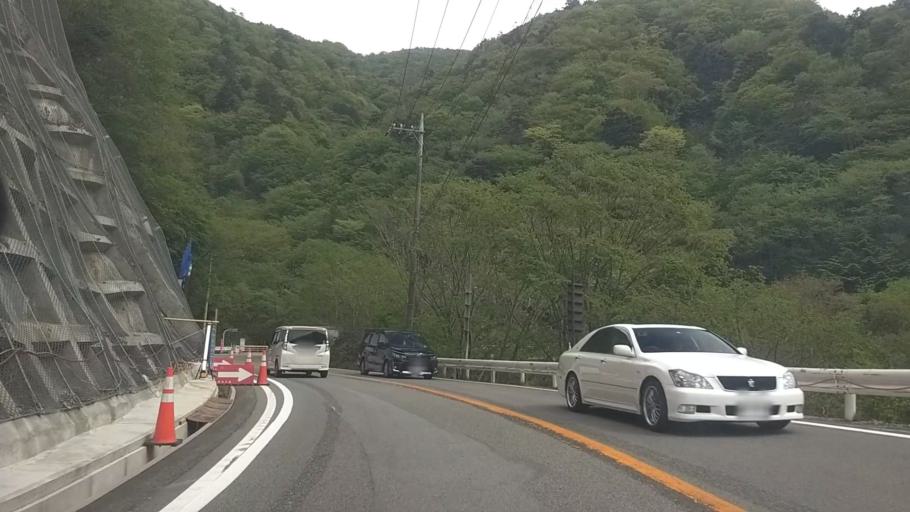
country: JP
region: Yamanashi
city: Fujikawaguchiko
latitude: 35.5092
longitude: 138.6160
